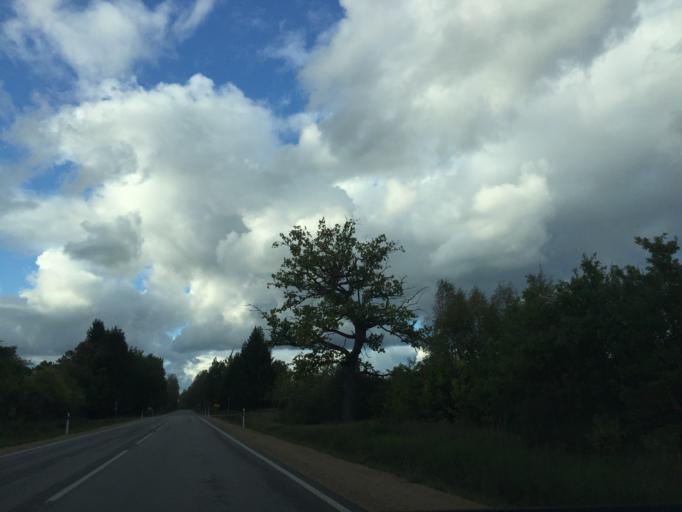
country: LV
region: Ligatne
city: Ligatne
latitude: 57.1756
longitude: 25.0406
